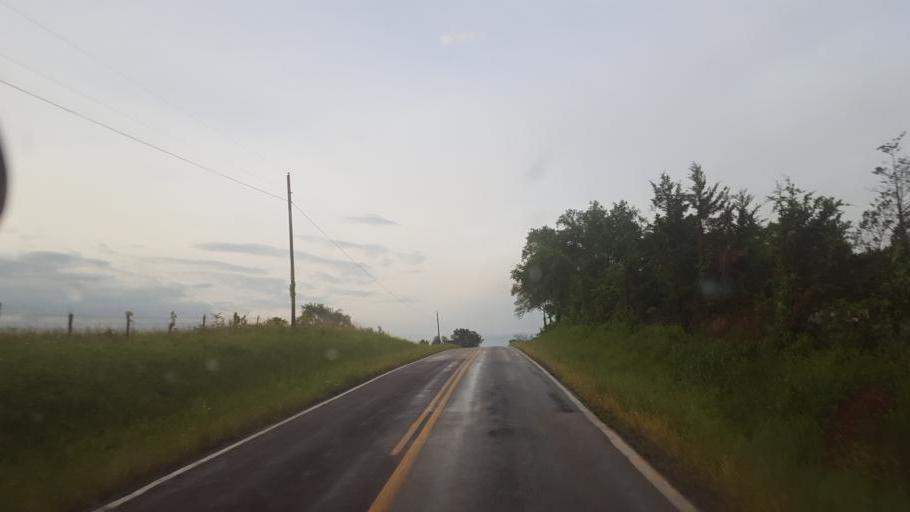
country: US
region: Missouri
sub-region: Moniteau County
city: California
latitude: 38.7132
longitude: -92.6343
